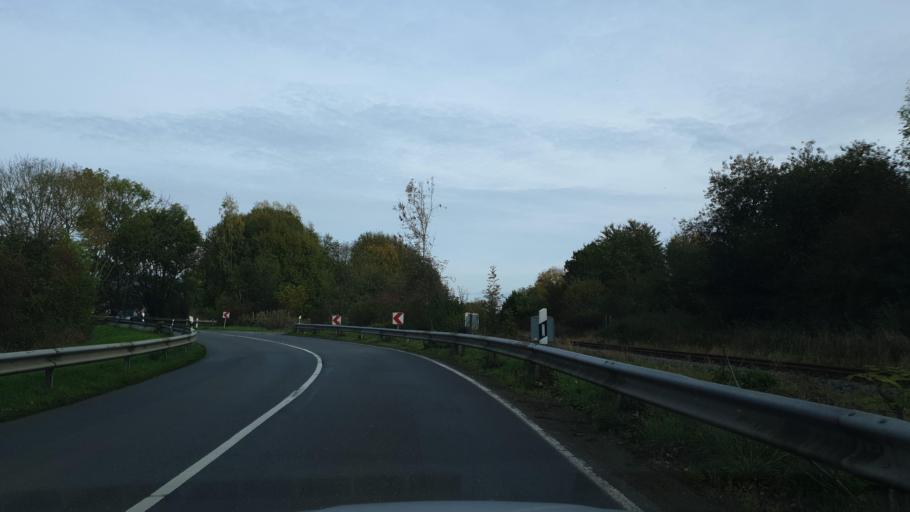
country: DE
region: Lower Saxony
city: Buckeburg
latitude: 52.1983
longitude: 8.9971
